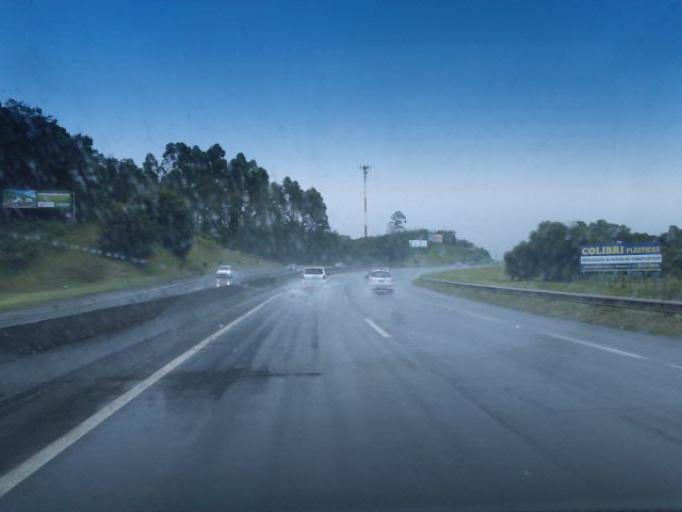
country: BR
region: Santa Catarina
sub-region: Joinville
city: Joinville
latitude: -26.4162
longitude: -48.8347
